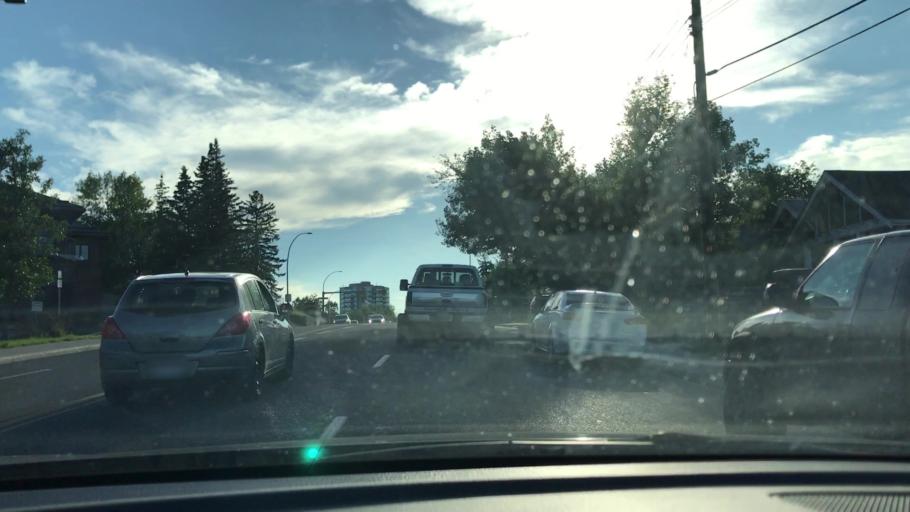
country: CA
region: Alberta
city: Calgary
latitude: 51.0378
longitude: -114.1092
